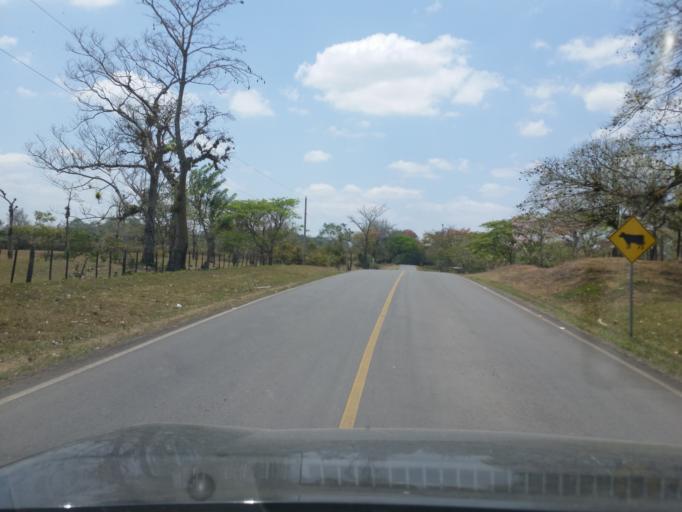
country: NI
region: Matagalpa
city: Muy Muy
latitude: 12.6441
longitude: -85.5365
